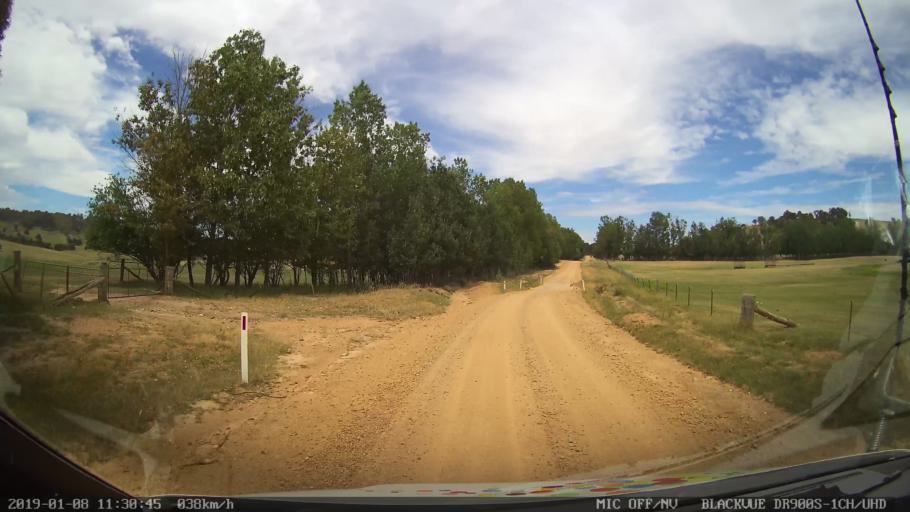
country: AU
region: New South Wales
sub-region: Guyra
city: Guyra
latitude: -30.3094
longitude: 151.5425
